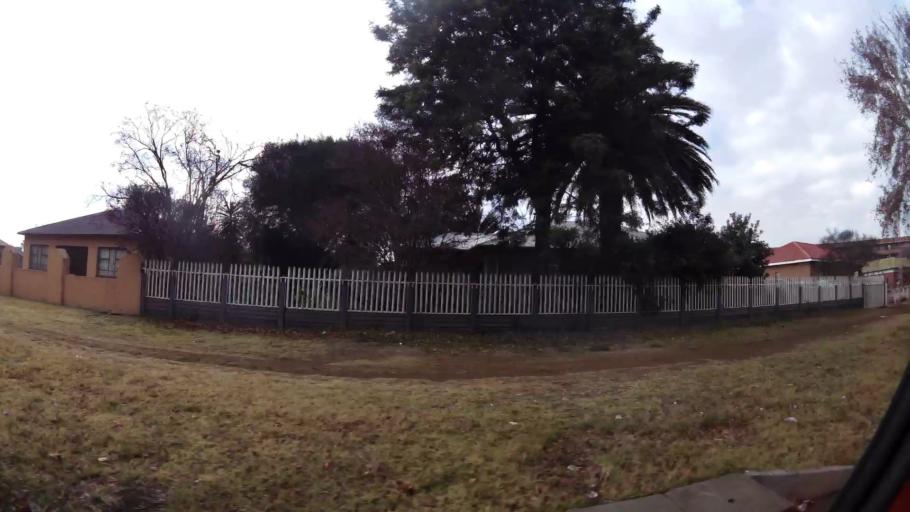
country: ZA
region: Gauteng
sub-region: Sedibeng District Municipality
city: Vanderbijlpark
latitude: -26.6871
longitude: 27.8153
